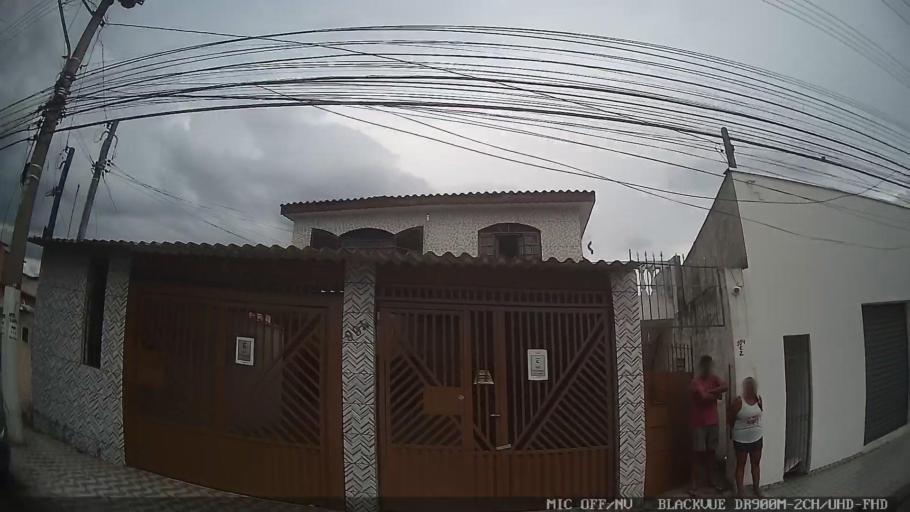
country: BR
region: Sao Paulo
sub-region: Suzano
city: Suzano
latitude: -23.5523
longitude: -46.2933
